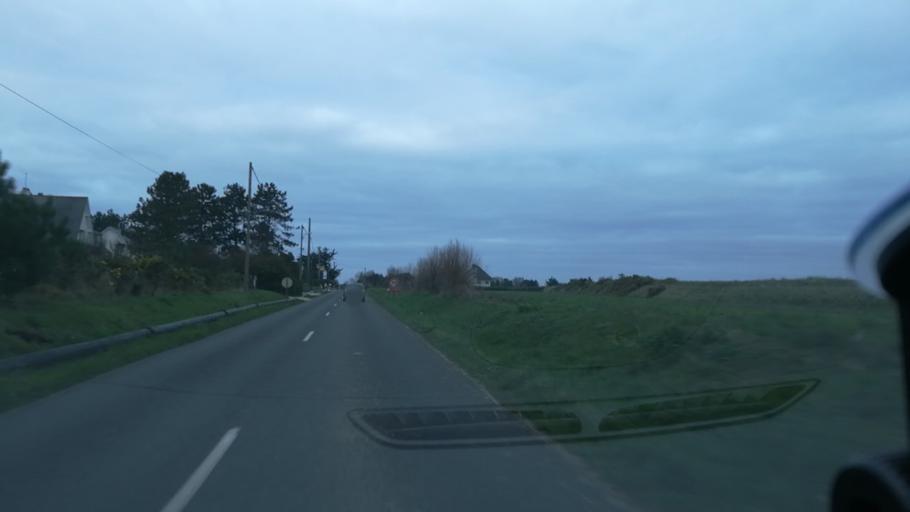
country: FR
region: Lower Normandy
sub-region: Departement de la Manche
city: Reville
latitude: 49.6066
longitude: -1.2583
